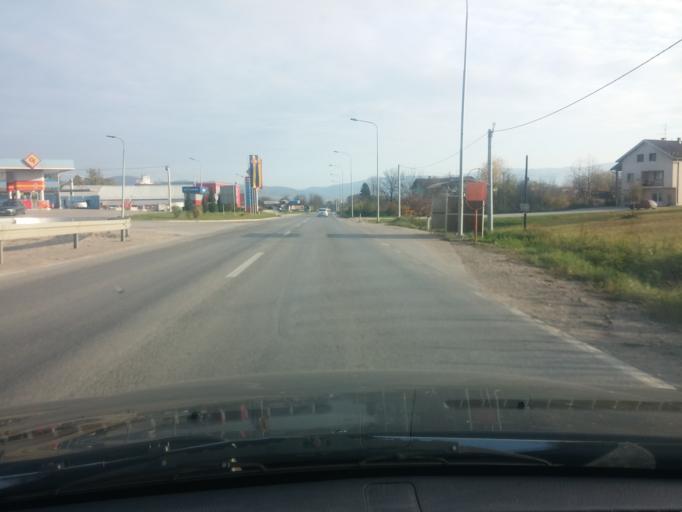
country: BA
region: Republika Srpska
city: Banja Luka
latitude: 44.8276
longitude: 17.1896
